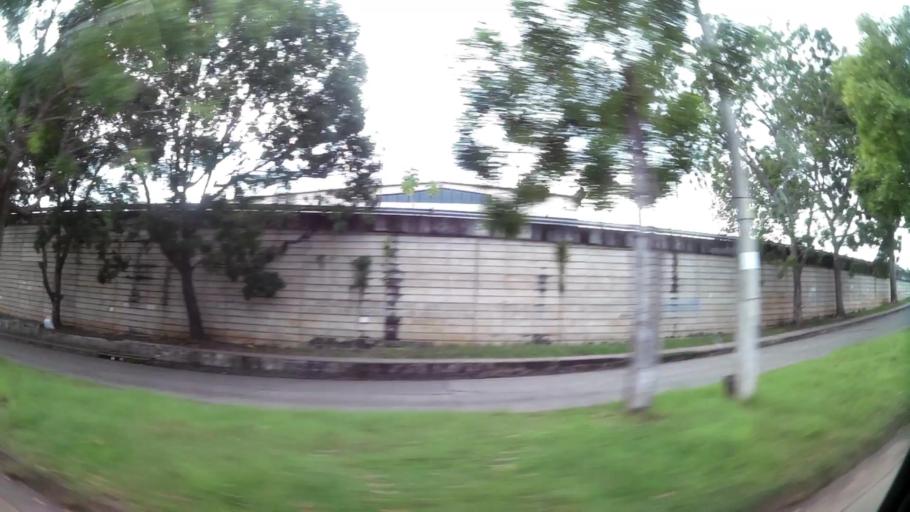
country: PA
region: Panama
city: Tocumen
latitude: 9.0988
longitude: -79.3877
